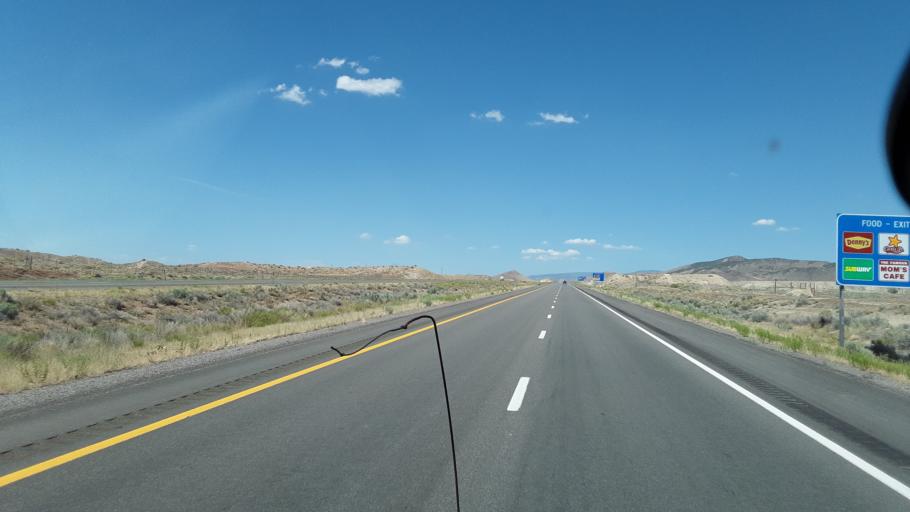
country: US
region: Utah
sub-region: Sevier County
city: Salina
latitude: 38.9174
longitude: -111.8796
